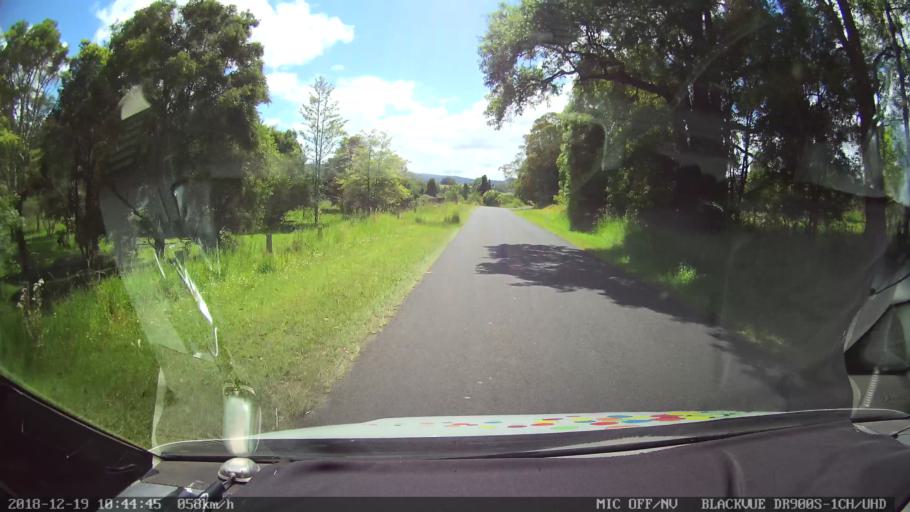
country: AU
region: New South Wales
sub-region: Lismore Municipality
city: Nimbin
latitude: -28.5950
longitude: 153.1837
